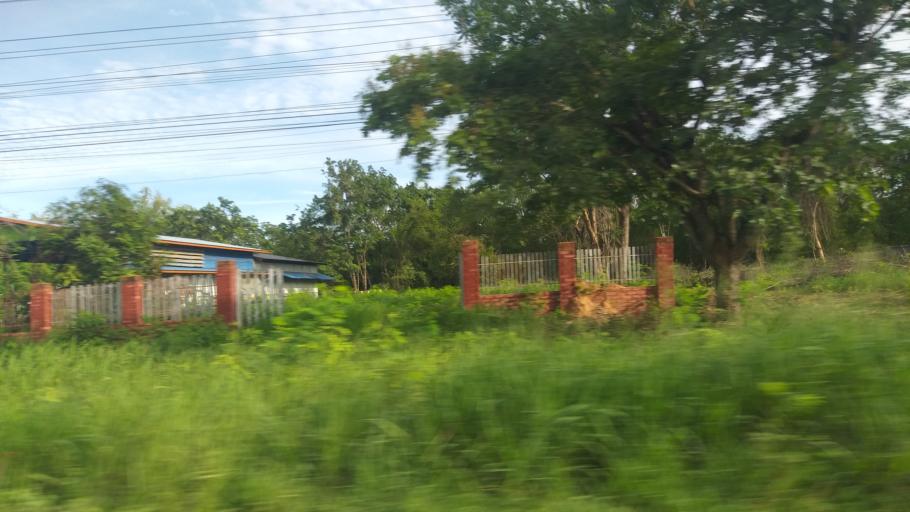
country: TH
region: Chaiyaphum
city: Ban Thaen
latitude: 16.3960
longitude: 102.3339
